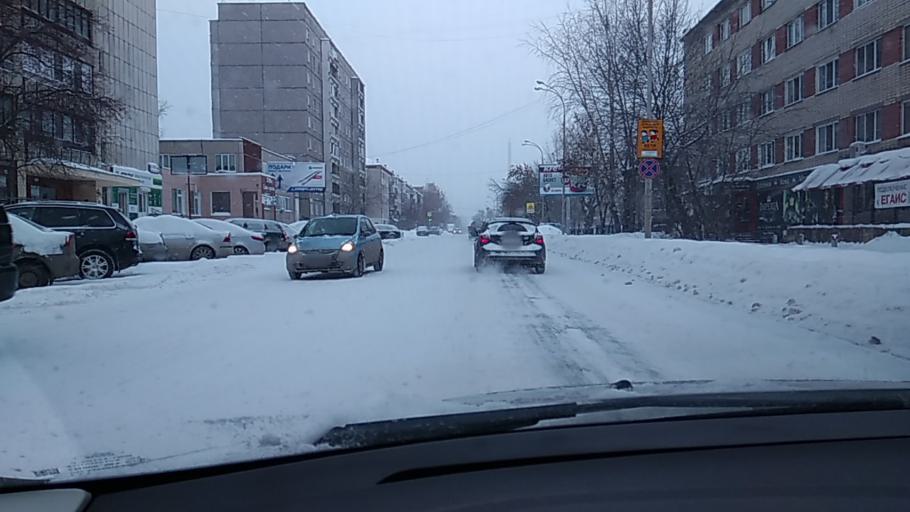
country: RU
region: Sverdlovsk
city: Yekaterinburg
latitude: 56.8094
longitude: 60.6129
